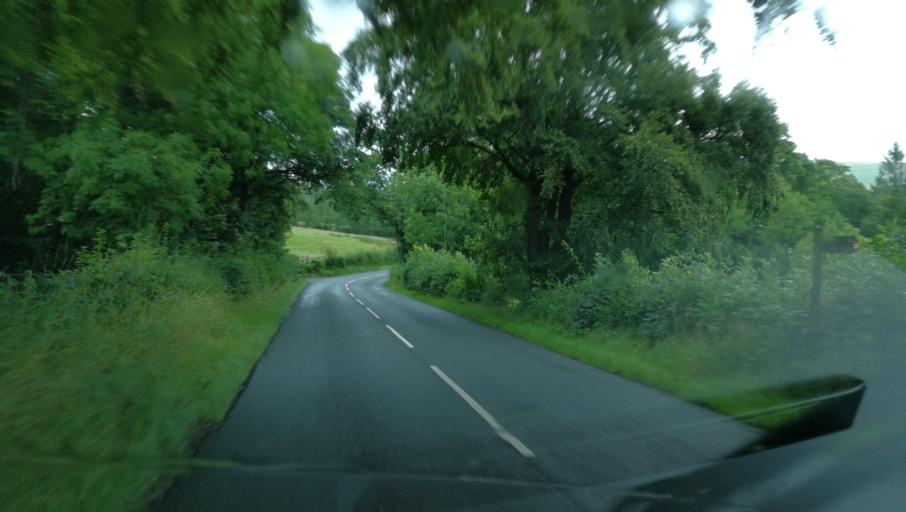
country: GB
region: England
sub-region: Cumbria
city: Penrith
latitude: 54.6039
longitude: -2.8451
